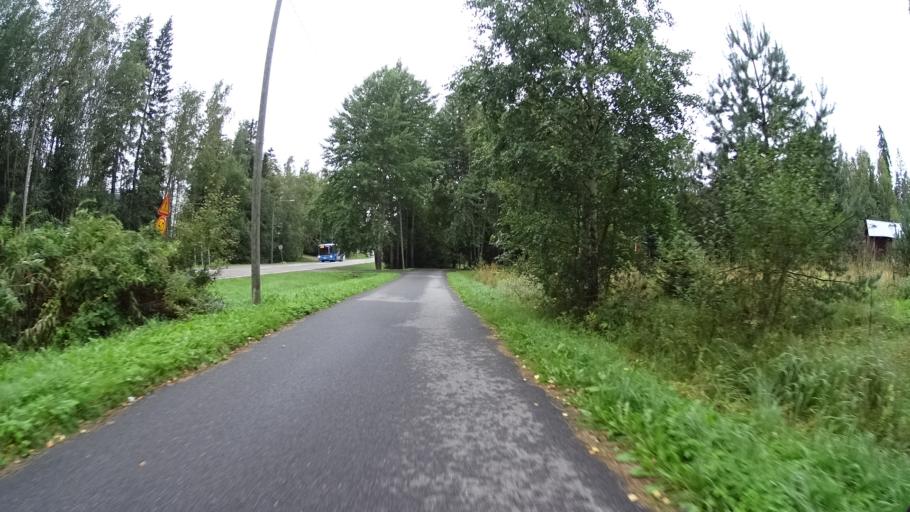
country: FI
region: Uusimaa
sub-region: Helsinki
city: Kauniainen
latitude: 60.2236
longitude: 24.6933
